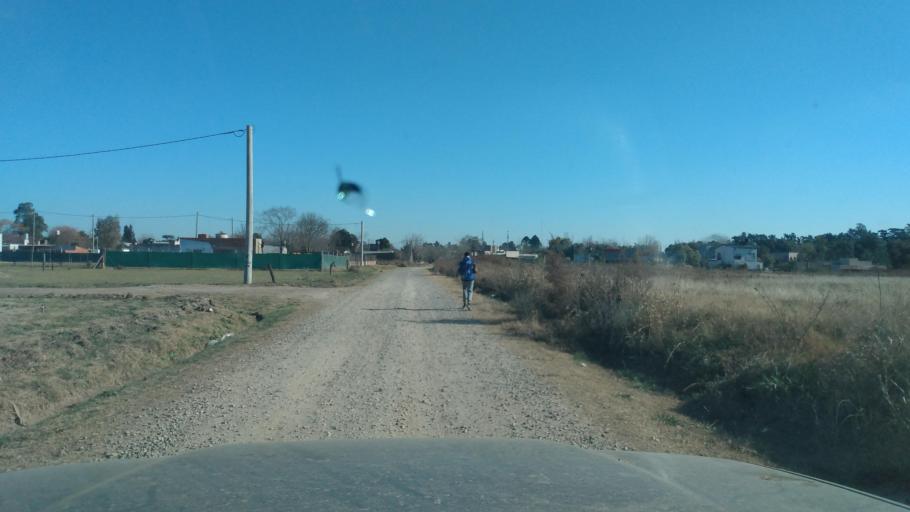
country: AR
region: Buenos Aires
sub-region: Partido de Lujan
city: Lujan
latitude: -34.5658
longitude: -59.0853
